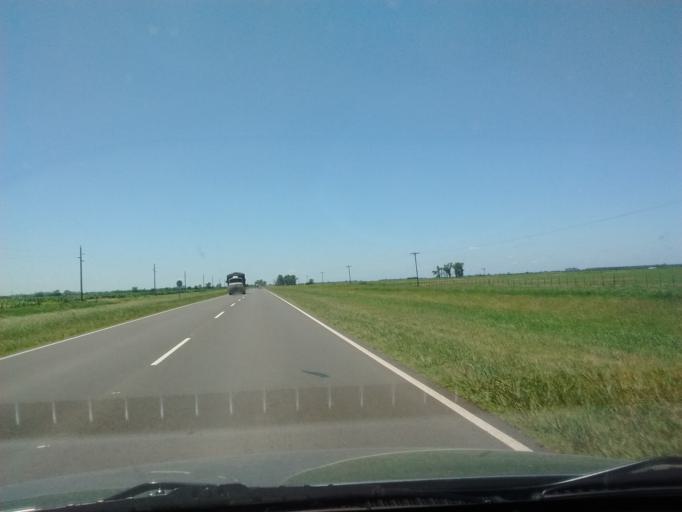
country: AR
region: Entre Rios
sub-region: Departamento de Gualeguay
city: Gualeguay
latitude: -33.0079
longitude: -59.4946
